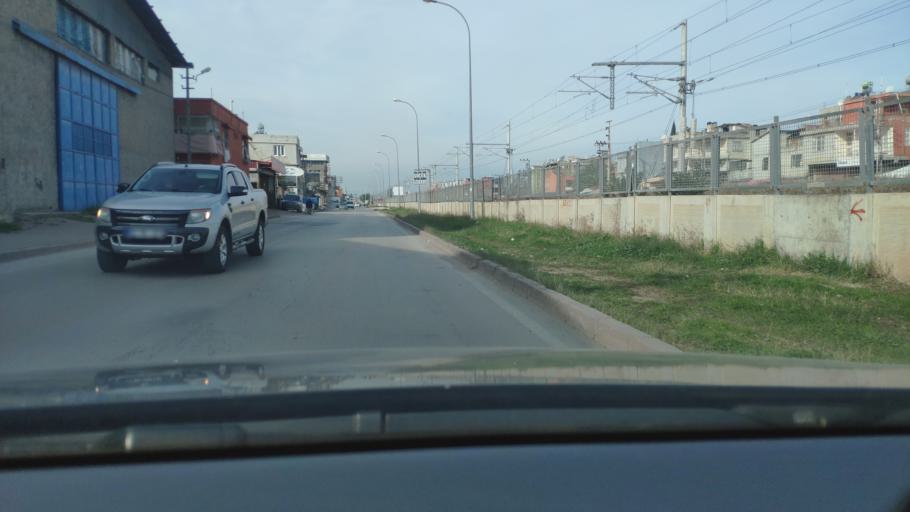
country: TR
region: Adana
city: Seyhan
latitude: 36.9975
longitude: 35.2717
